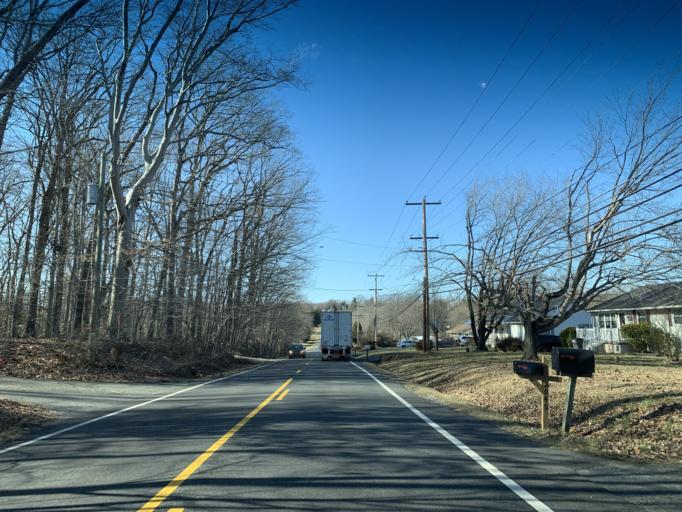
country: US
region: Maryland
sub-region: Cecil County
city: North East
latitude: 39.6633
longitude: -75.8942
